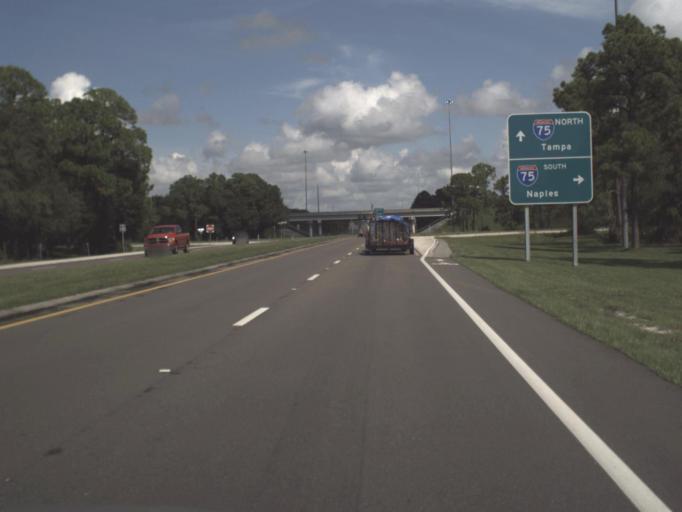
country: US
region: Florida
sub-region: Sarasota County
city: North Port
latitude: 27.0958
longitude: -82.1554
